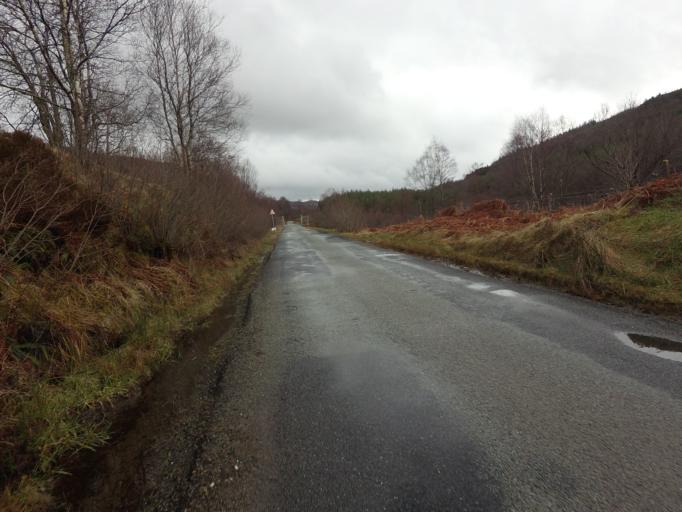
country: GB
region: Scotland
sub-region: West Dunbartonshire
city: Balloch
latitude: 56.2443
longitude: -4.5748
